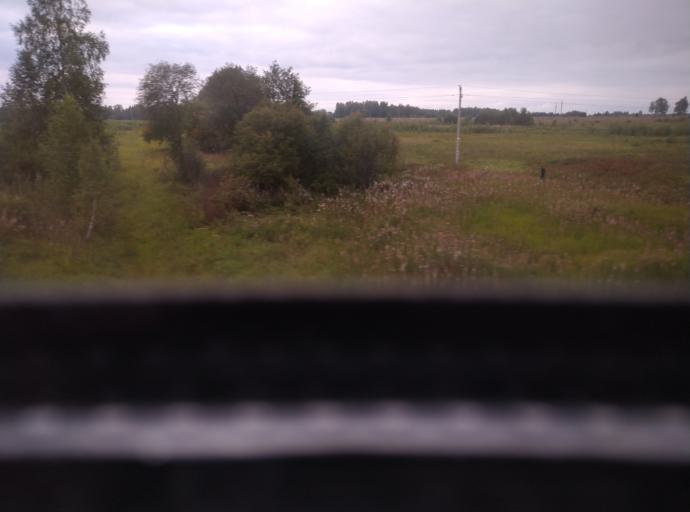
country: RU
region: Kostroma
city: Nerekhta
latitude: 57.4534
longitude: 40.4471
